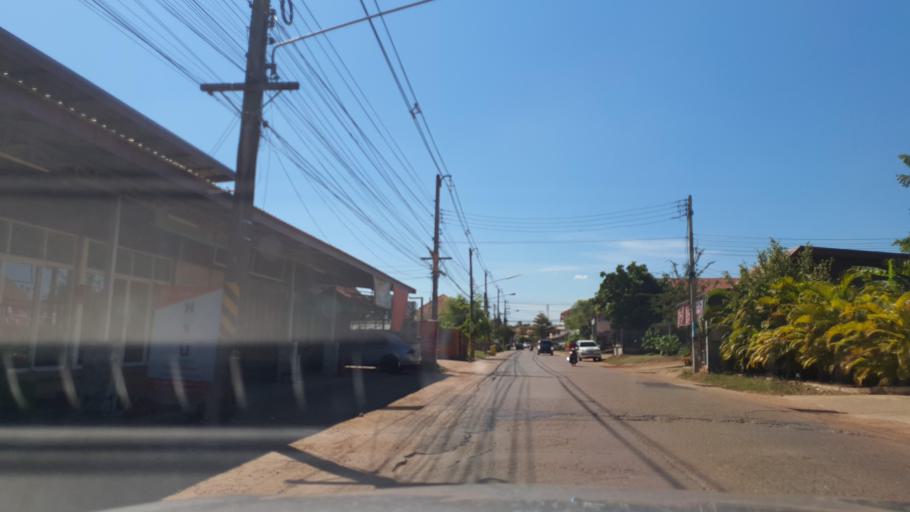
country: TH
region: Sakon Nakhon
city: Sakon Nakhon
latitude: 17.1613
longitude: 104.1224
